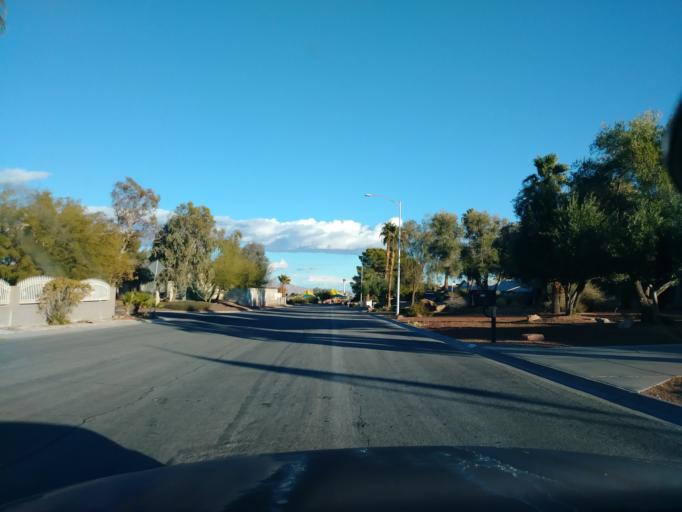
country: US
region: Nevada
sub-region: Clark County
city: Spring Valley
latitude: 36.1491
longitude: -115.2406
